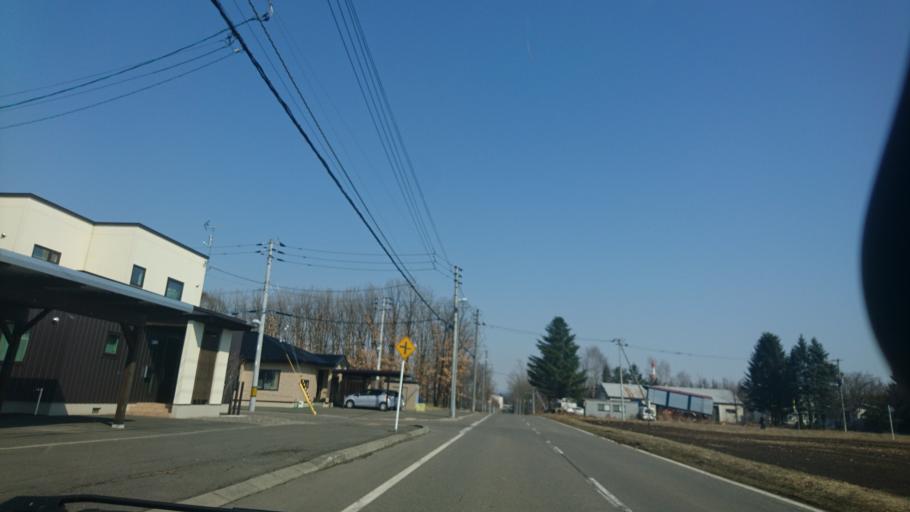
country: JP
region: Hokkaido
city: Obihiro
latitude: 42.9147
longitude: 143.0766
